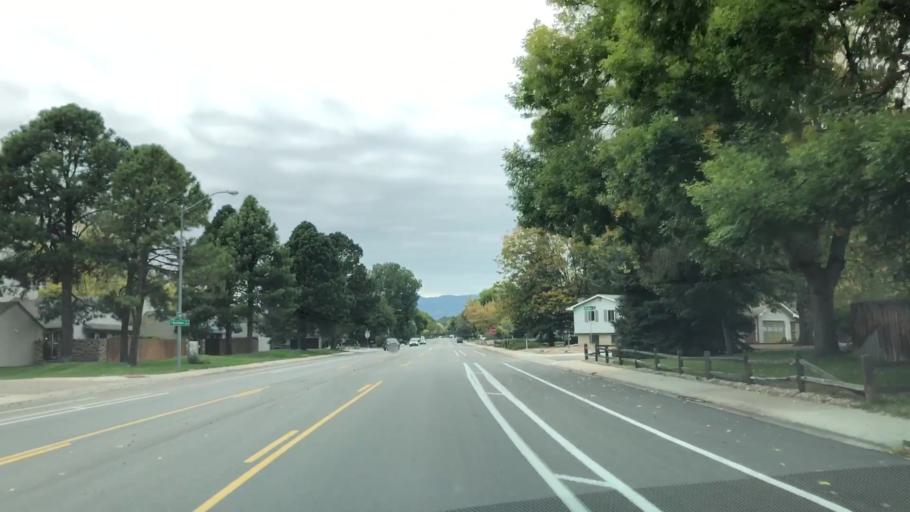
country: US
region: Colorado
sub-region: Larimer County
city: Fort Collins
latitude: 40.5458
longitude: -105.0675
